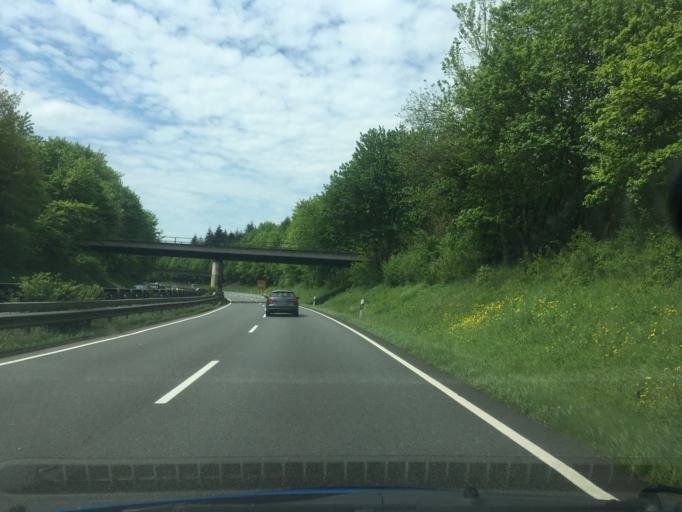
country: DE
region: Lower Saxony
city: Adendorf
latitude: 53.2677
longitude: 10.4377
